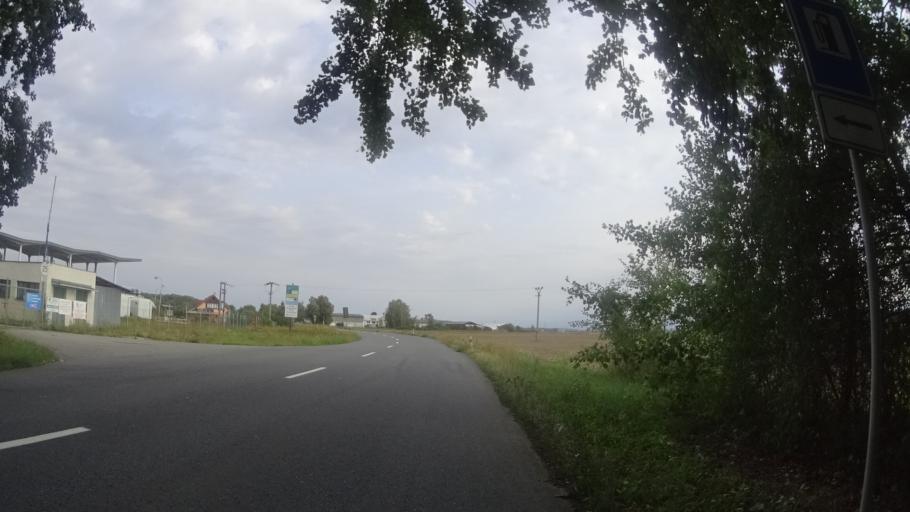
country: CZ
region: Zlin
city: Chropyne
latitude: 49.3337
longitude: 17.3851
